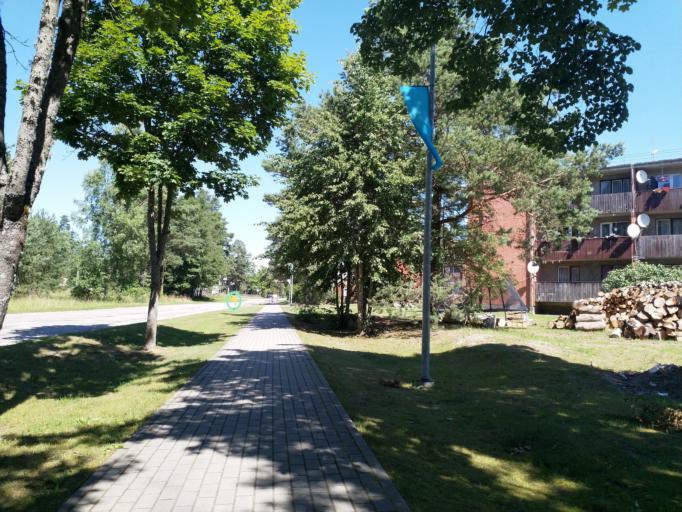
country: LV
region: Dundaga
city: Dundaga
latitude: 57.7358
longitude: 22.5812
